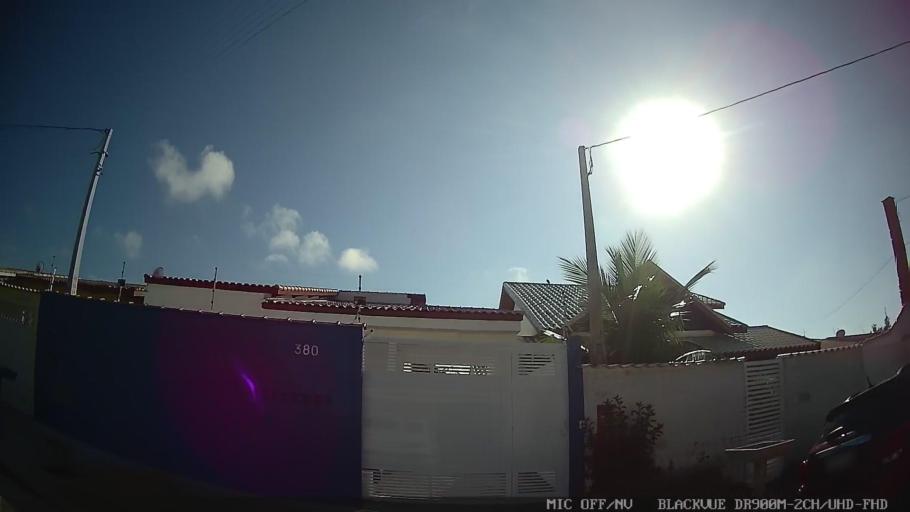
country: BR
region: Sao Paulo
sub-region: Peruibe
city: Peruibe
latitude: -24.2717
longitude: -46.9356
